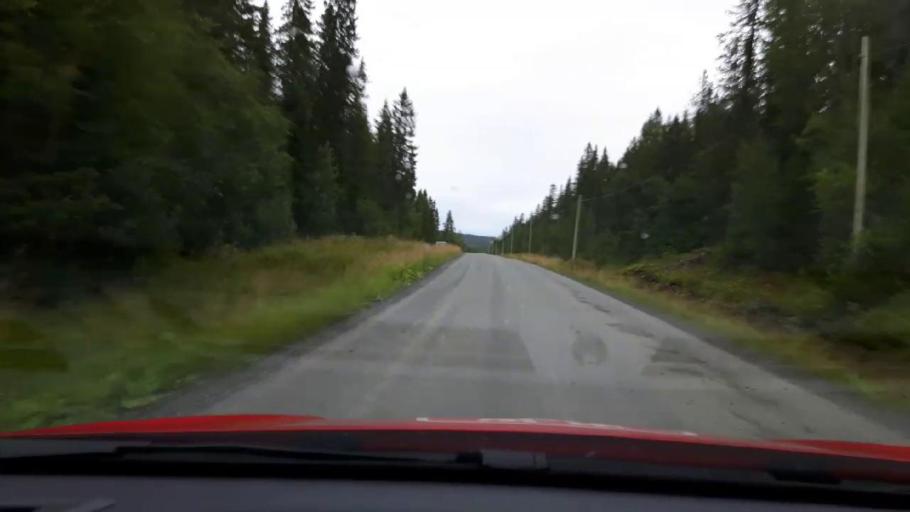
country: SE
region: Jaemtland
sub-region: Are Kommun
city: Jarpen
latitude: 63.4285
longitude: 13.3212
